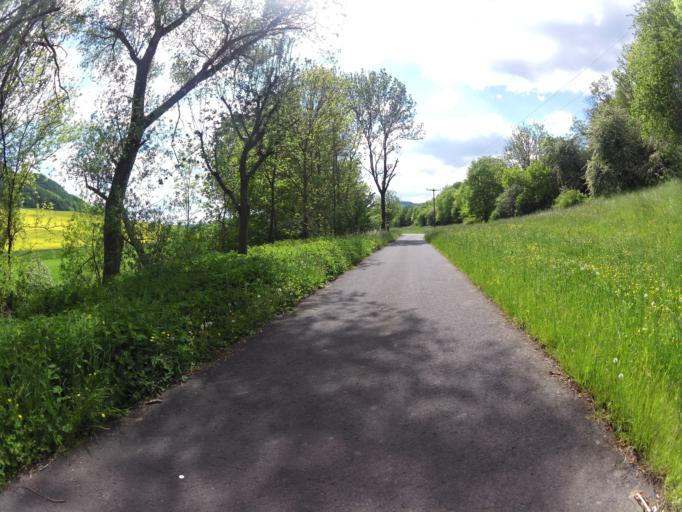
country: DE
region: Thuringia
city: Treffurt
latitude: 51.1209
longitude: 10.2335
